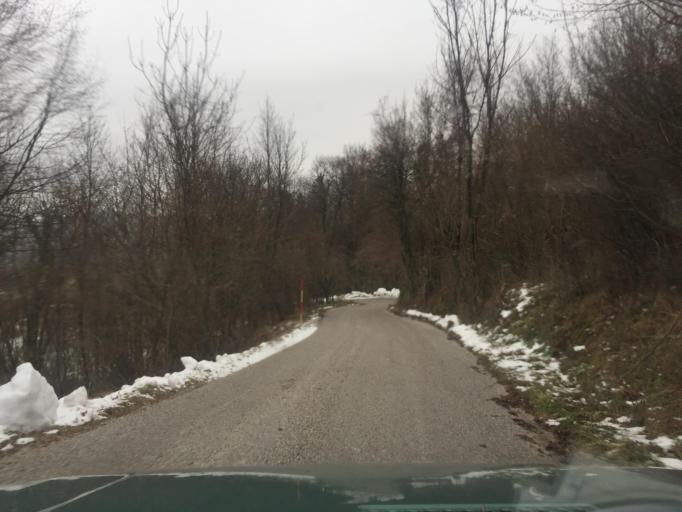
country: SI
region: Kanal
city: Kanal
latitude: 46.0719
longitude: 13.6907
